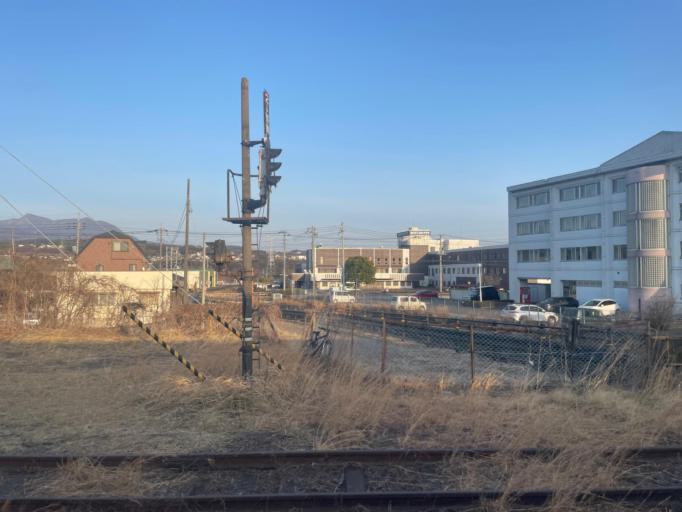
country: JP
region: Gunma
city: Shibukawa
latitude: 36.4935
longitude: 139.0097
